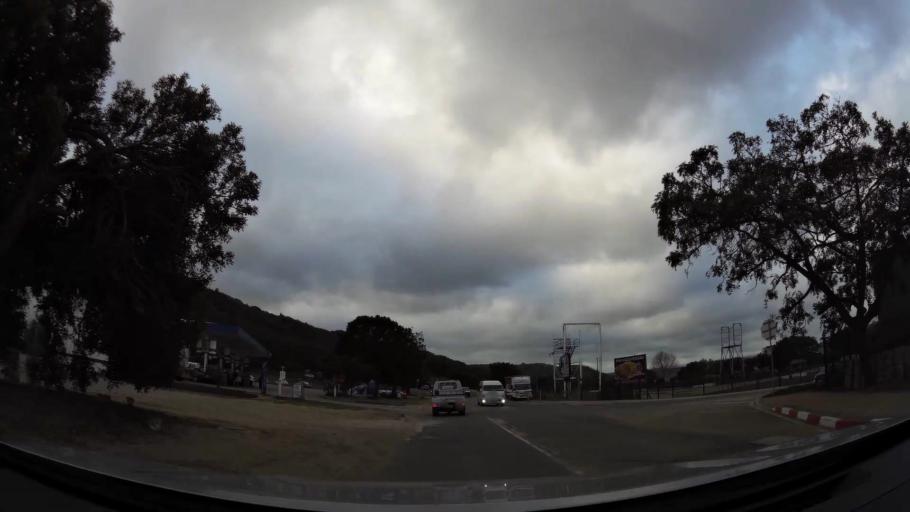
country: ZA
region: Western Cape
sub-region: Eden District Municipality
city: Plettenberg Bay
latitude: -34.0416
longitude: 23.3705
